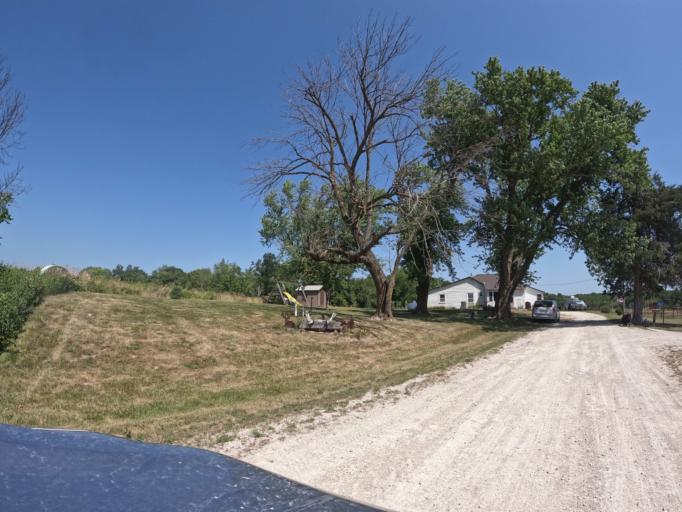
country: US
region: Iowa
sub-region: Henry County
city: Mount Pleasant
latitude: 40.8915
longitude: -91.5743
